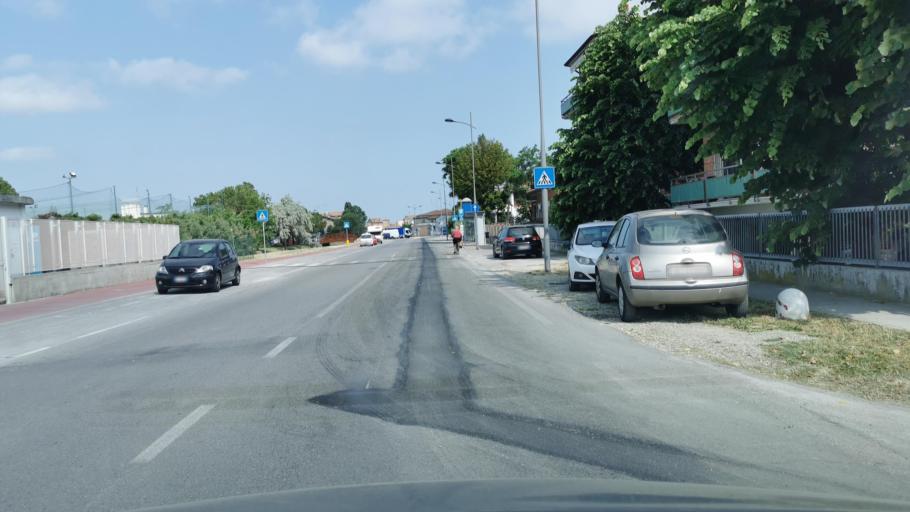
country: IT
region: Emilia-Romagna
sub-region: Provincia di Ferrara
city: Comacchio
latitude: 44.6901
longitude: 12.1878
